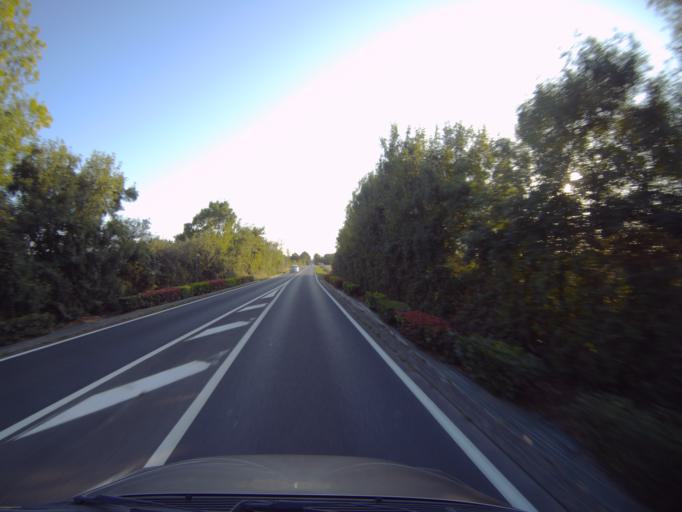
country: FR
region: Pays de la Loire
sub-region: Departement de la Vendee
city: Montaigu
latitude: 46.9992
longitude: -1.2905
